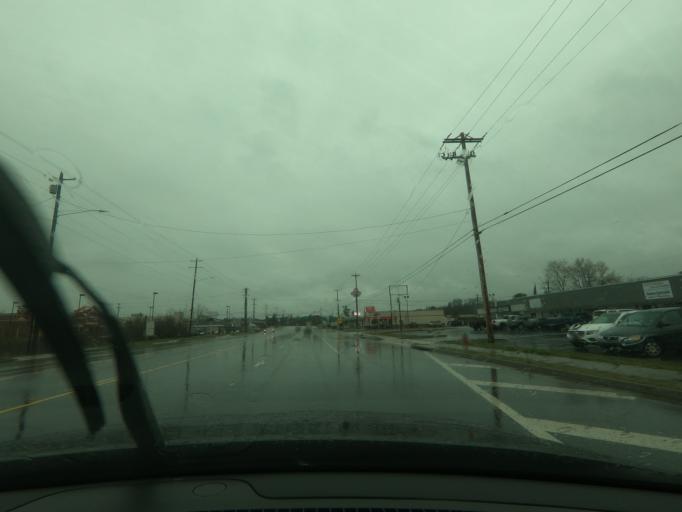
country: US
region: Georgia
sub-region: Gordon County
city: Calhoun
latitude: 34.5119
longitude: -84.9220
